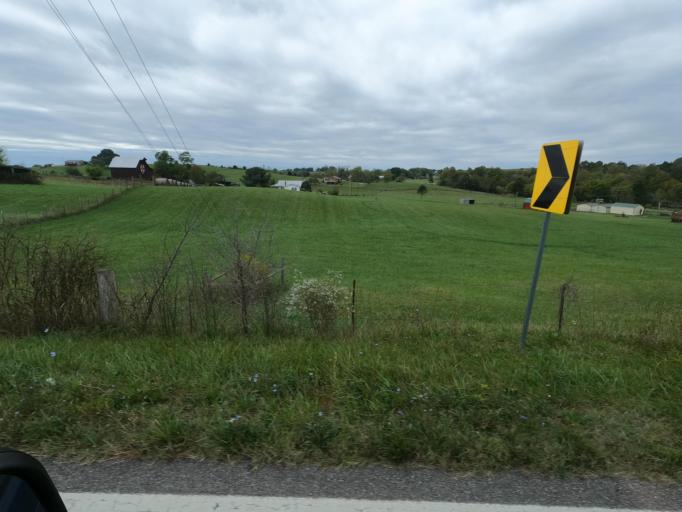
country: US
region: Tennessee
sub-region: Washington County
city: Jonesborough
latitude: 36.2429
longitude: -82.5570
